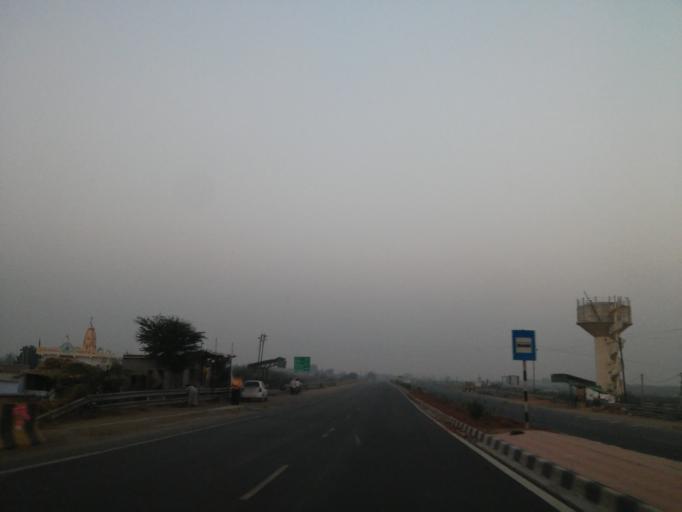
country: IN
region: Gujarat
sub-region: Surendranagar
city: Dhrangadhra
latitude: 23.0018
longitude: 71.3916
